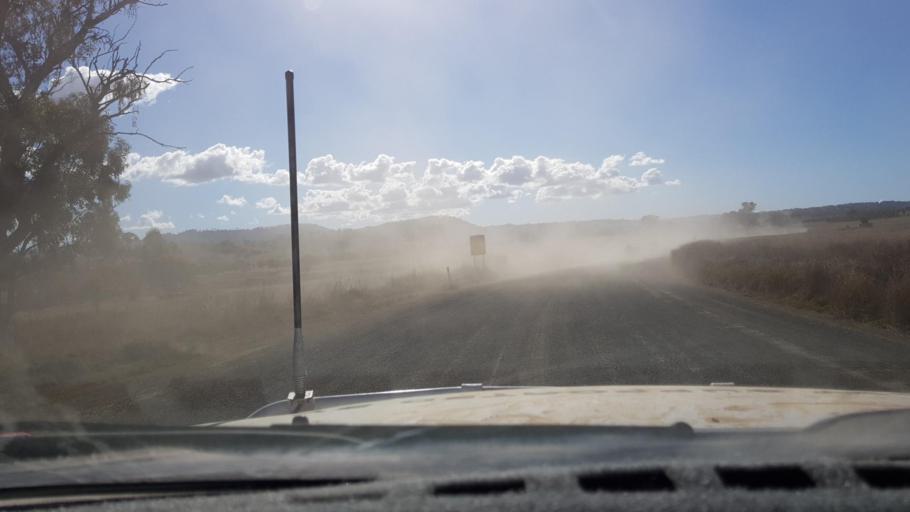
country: AU
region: New South Wales
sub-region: Narrabri
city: Blair Athol
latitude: -30.6762
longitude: 150.4445
